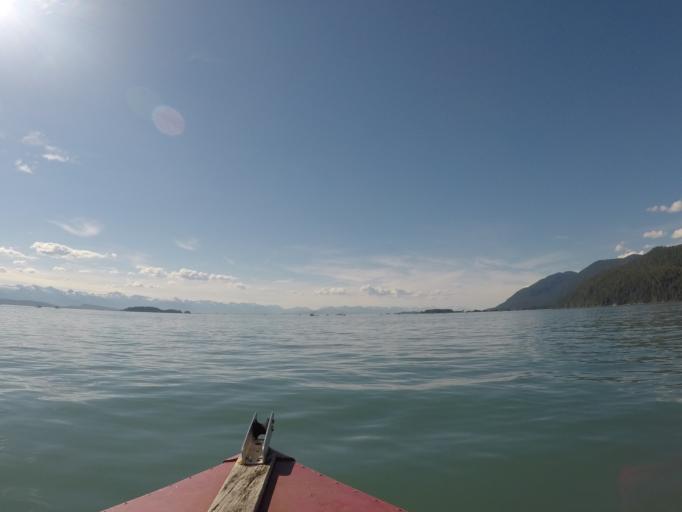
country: US
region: Alaska
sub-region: Juneau City and Borough
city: Juneau
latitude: 58.4924
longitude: -134.8116
